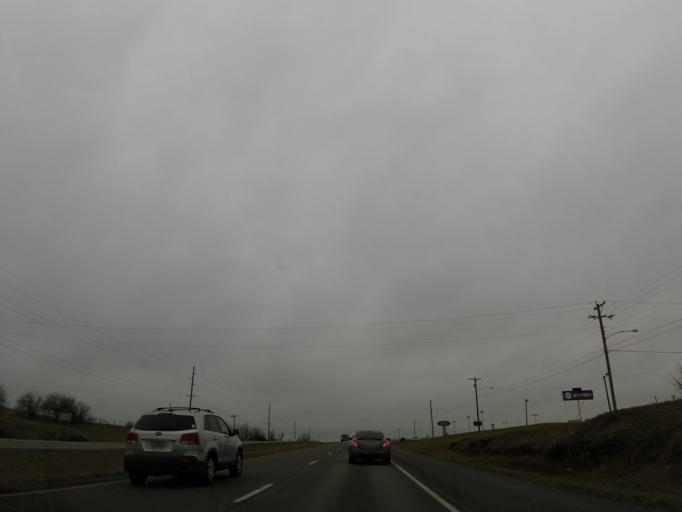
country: US
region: Kentucky
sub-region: Boyle County
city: Danville
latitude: 37.6472
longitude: -84.8031
